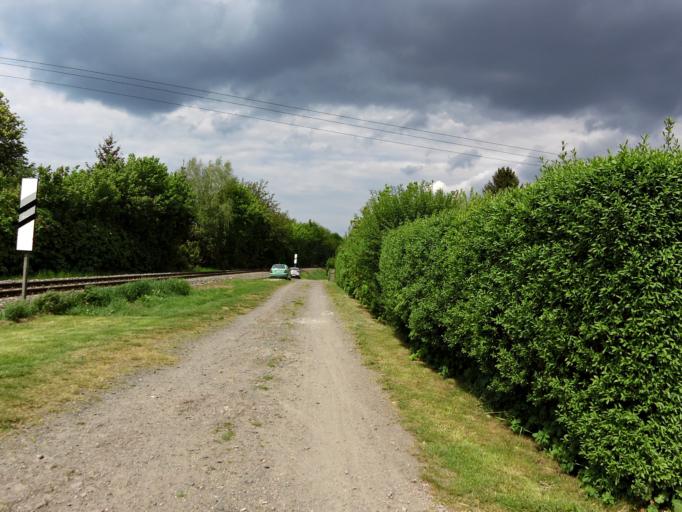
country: DE
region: Thuringia
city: Gotha
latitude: 50.9299
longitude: 10.6992
